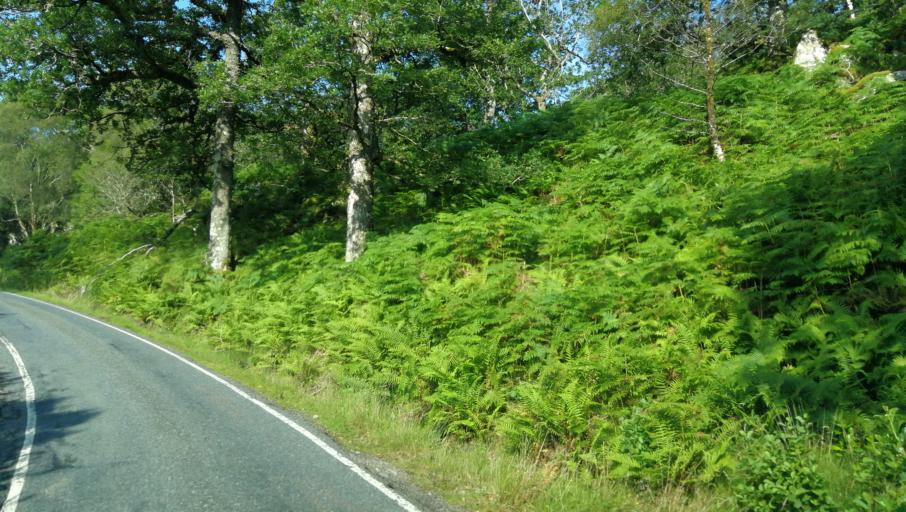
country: GB
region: Scotland
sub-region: Argyll and Bute
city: Isle Of Mull
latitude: 56.6796
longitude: -5.8339
